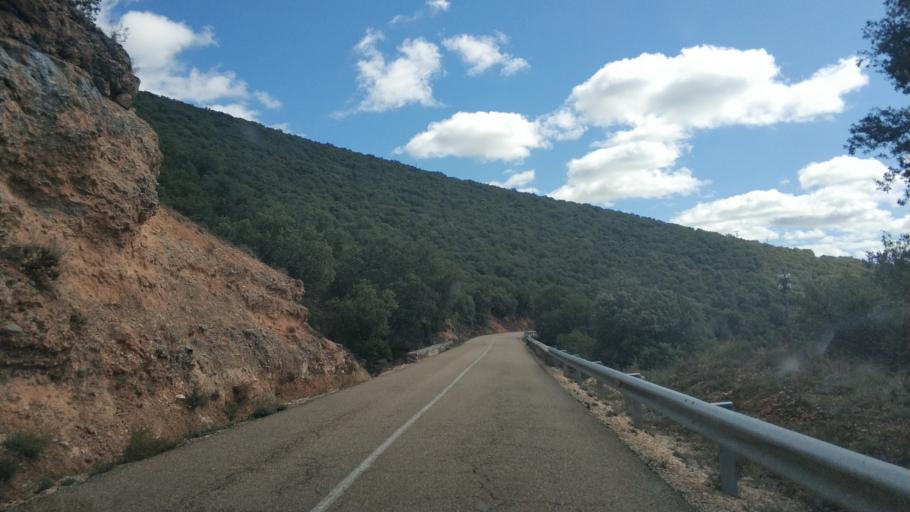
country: ES
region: Castille and Leon
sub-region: Provincia de Burgos
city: Retuerta
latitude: 42.0506
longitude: -3.4928
